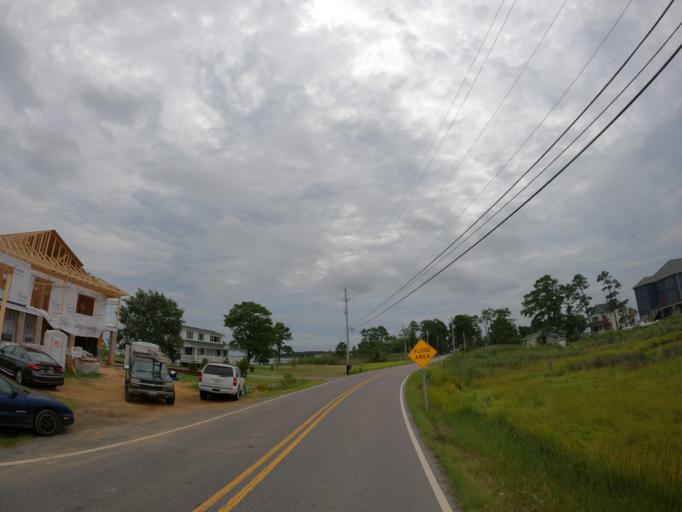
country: US
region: Maryland
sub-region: Saint Mary's County
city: Lexington Park
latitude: 38.1344
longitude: -76.4967
